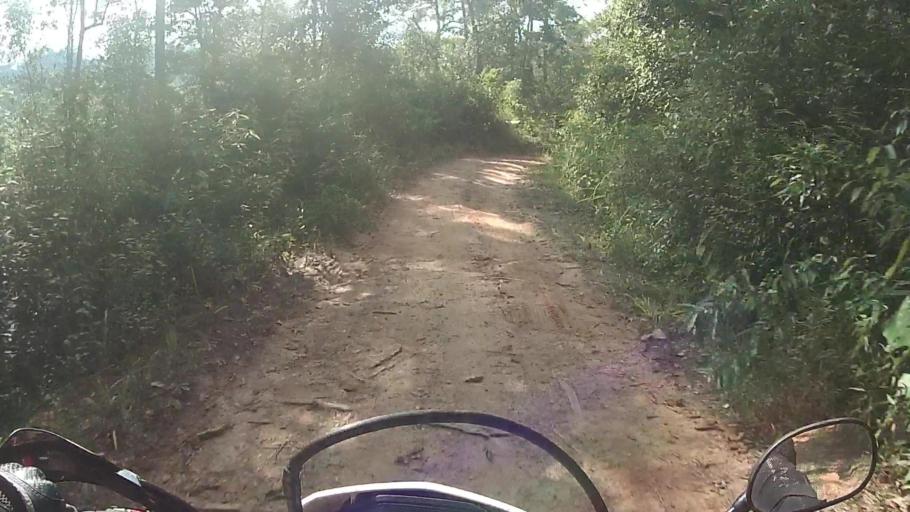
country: TH
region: Chiang Mai
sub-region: Amphoe Chiang Dao
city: Chiang Dao
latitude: 19.3553
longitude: 98.8227
